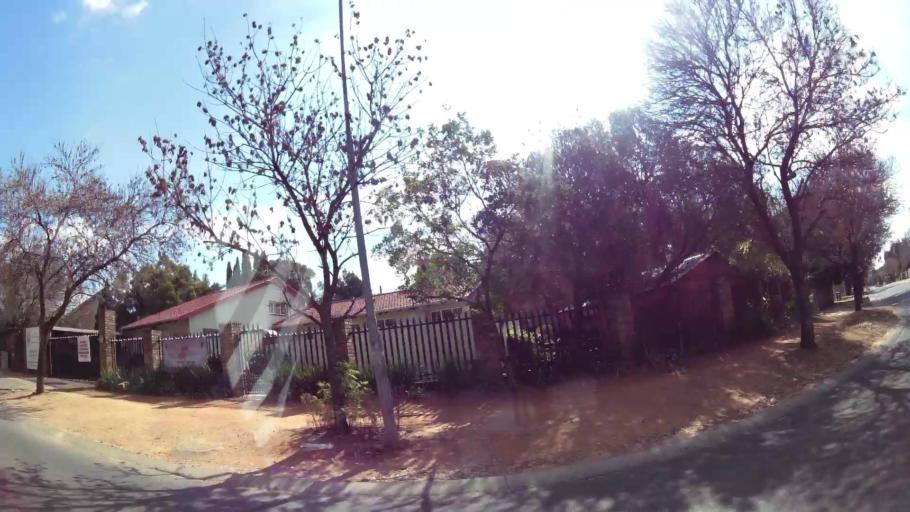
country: ZA
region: Gauteng
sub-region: West Rand District Municipality
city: Muldersdriseloop
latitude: -26.0639
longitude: 27.9611
